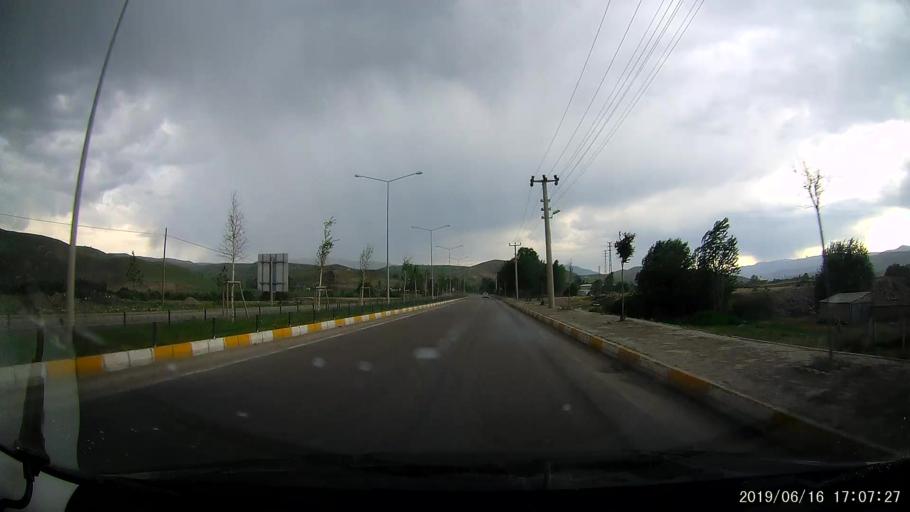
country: TR
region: Erzurum
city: Askale
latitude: 39.9176
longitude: 40.6757
